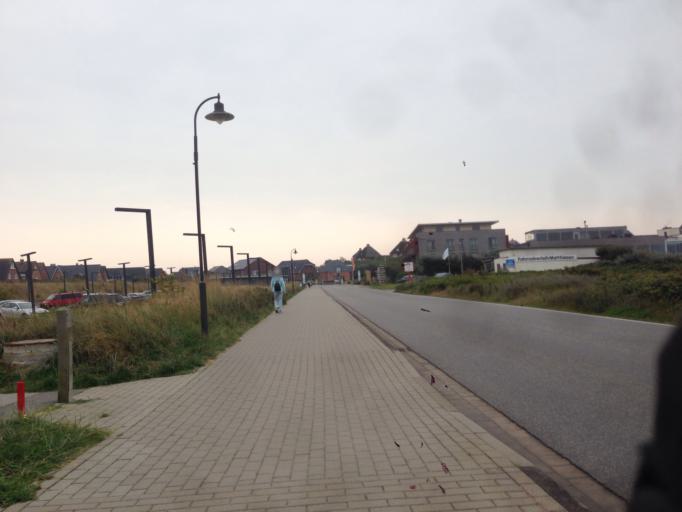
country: DE
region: Schleswig-Holstein
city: Norddorf
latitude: 54.7595
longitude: 8.2860
